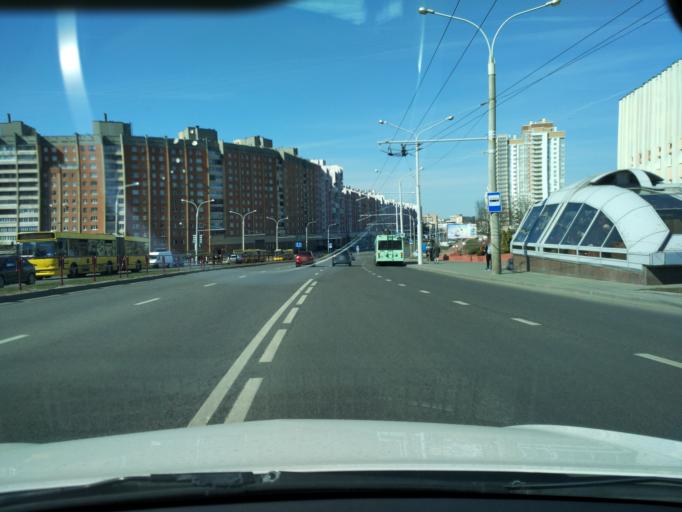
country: BY
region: Minsk
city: Minsk
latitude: 53.8747
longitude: 27.5692
